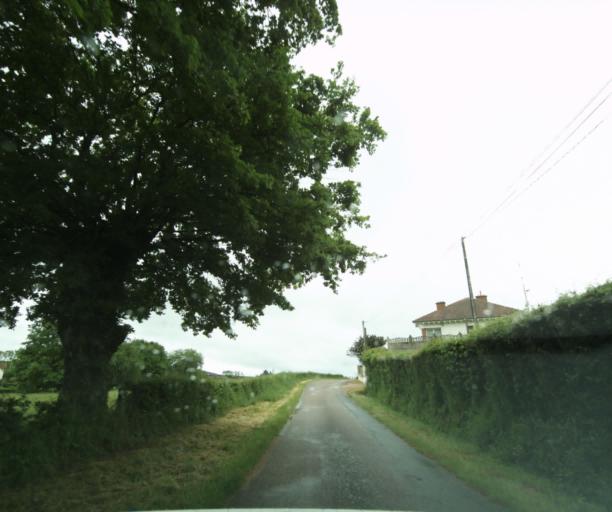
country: FR
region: Bourgogne
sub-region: Departement de Saone-et-Loire
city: Charolles
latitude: 46.4796
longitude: 4.4362
